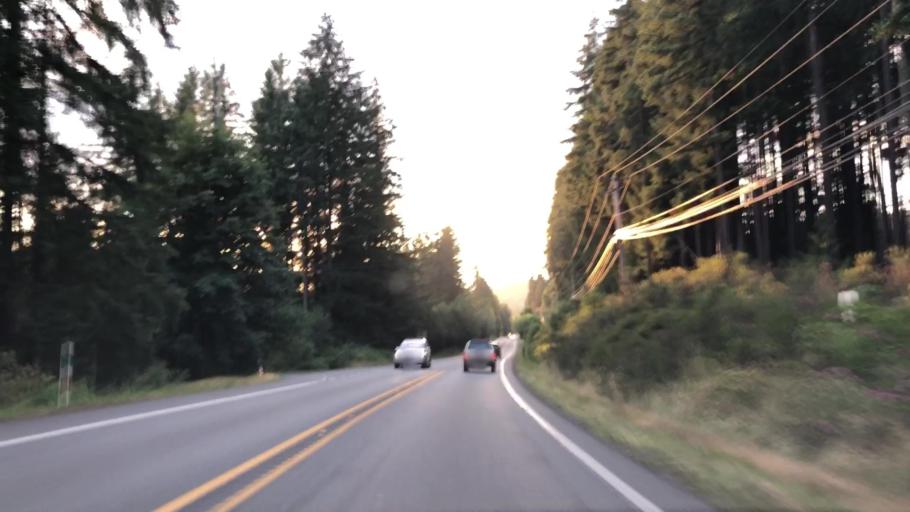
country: US
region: Washington
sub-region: King County
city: Union Hill-Novelty Hill
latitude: 47.6469
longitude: -122.0402
